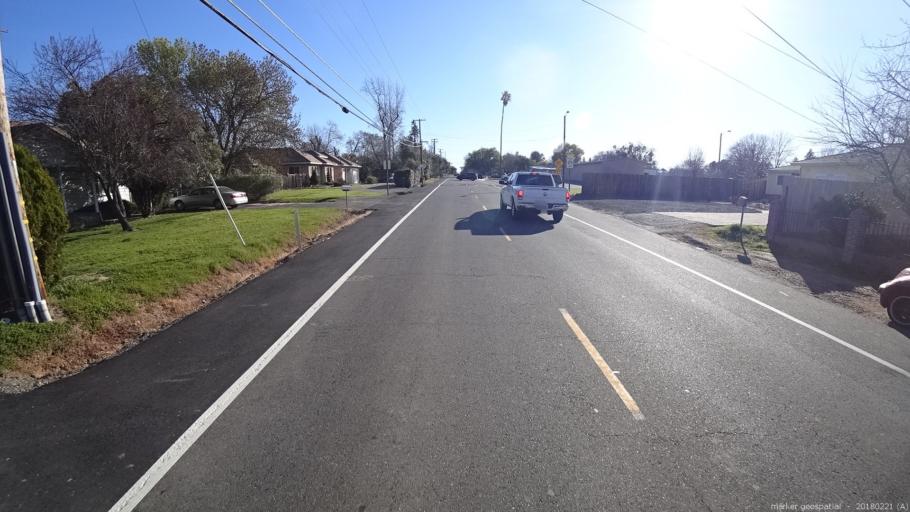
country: US
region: California
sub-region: Sacramento County
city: Orangevale
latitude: 38.6859
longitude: -121.2328
